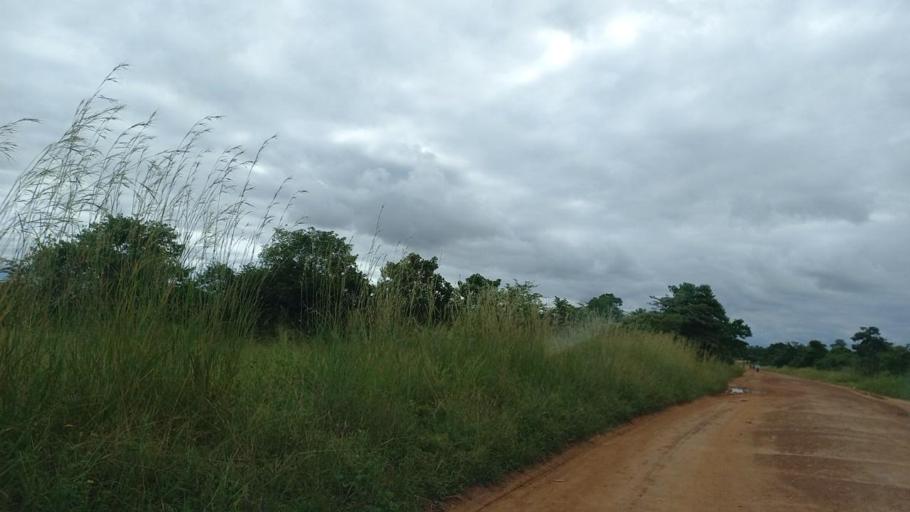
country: ZM
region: Lusaka
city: Chongwe
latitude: -15.4561
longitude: 28.8600
